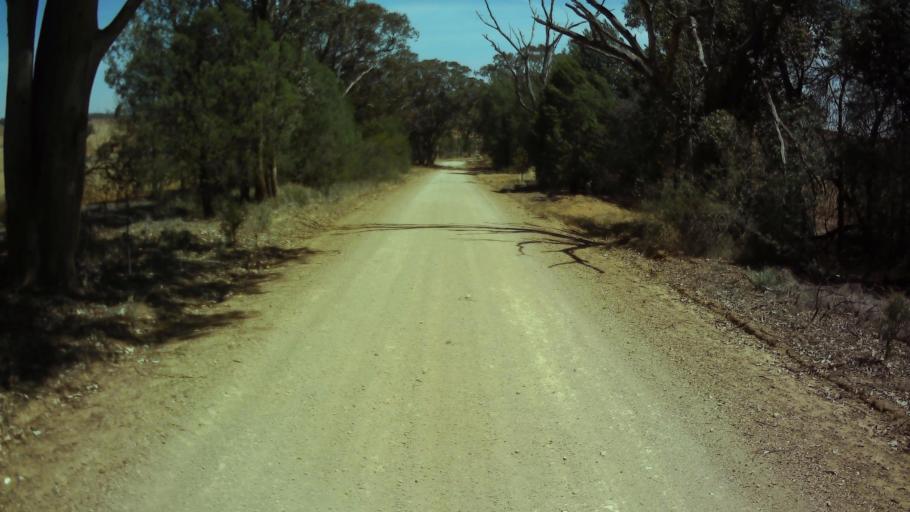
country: AU
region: New South Wales
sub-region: Weddin
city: Grenfell
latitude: -33.9205
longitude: 148.1786
